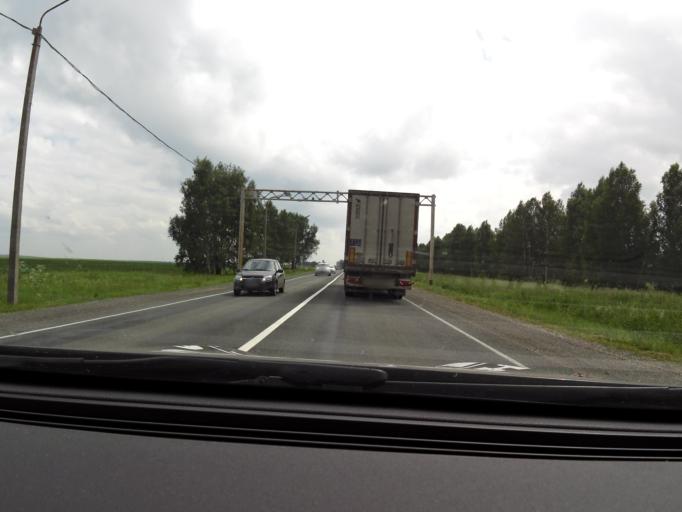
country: RU
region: Perm
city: Suksun
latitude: 56.9490
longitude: 57.5289
